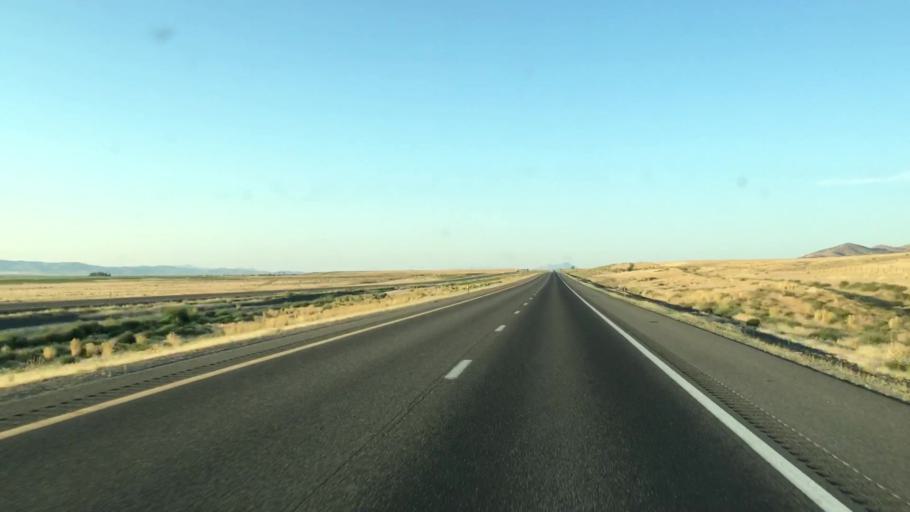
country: US
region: Nevada
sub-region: Humboldt County
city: Winnemucca
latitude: 40.7628
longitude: -118.0154
